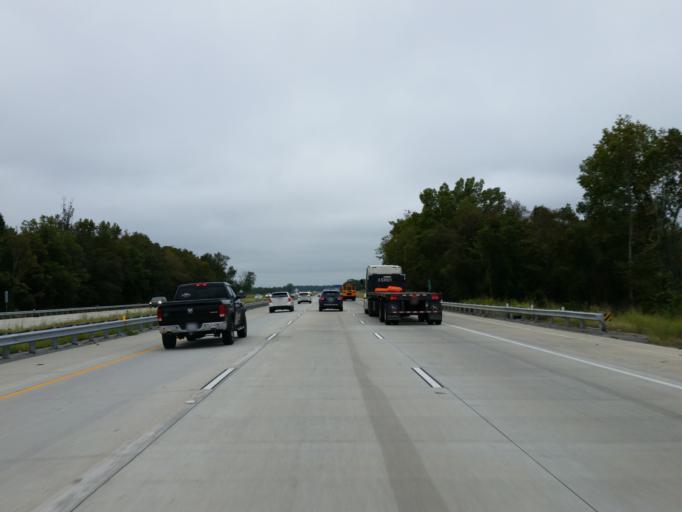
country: US
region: Georgia
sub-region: Dooly County
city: Vienna
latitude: 32.0535
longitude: -83.7638
